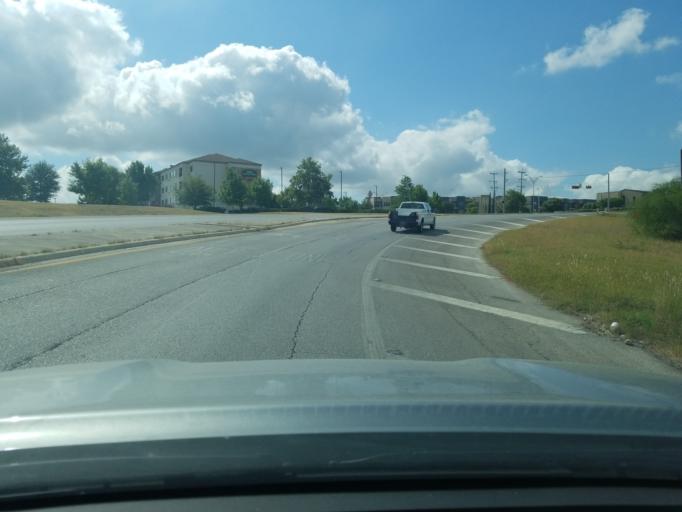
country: US
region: Texas
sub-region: Bexar County
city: Hollywood Park
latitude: 29.6149
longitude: -98.4655
